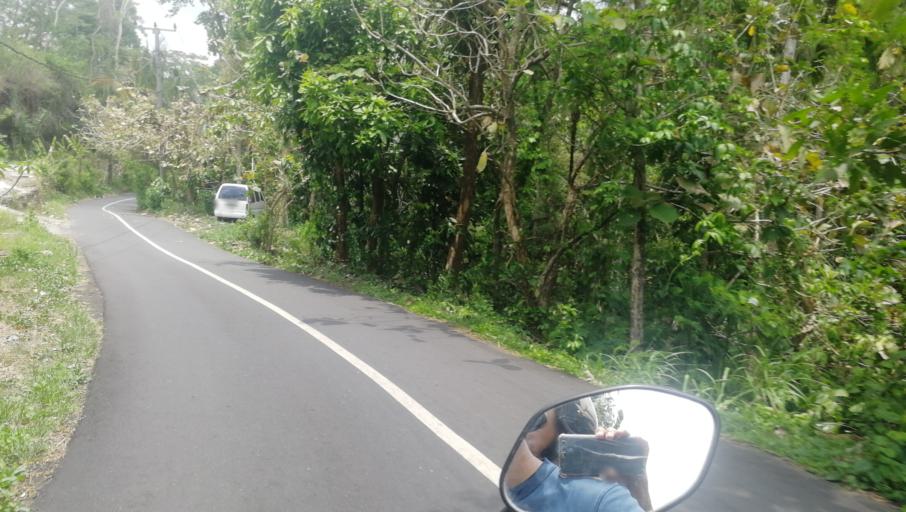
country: ID
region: Bali
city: Banjar Pedawa
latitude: -8.2654
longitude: 115.0243
